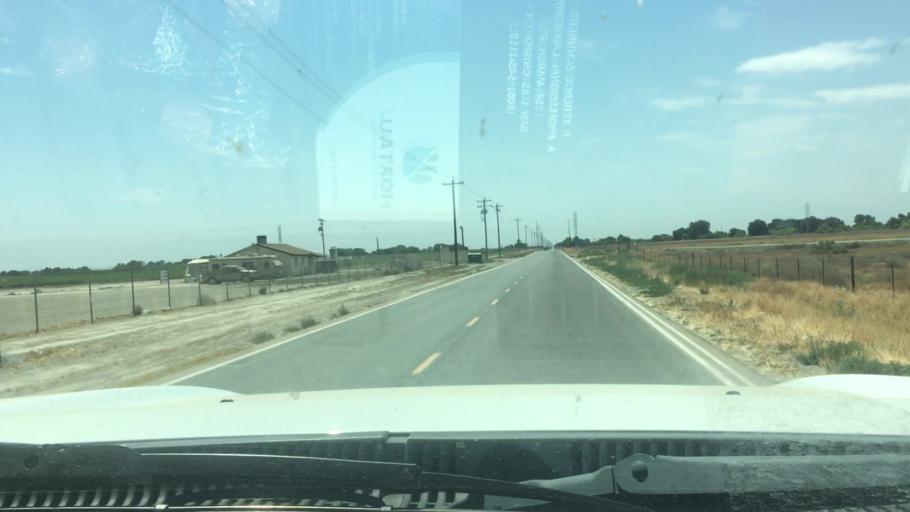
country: US
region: California
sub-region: Kings County
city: Corcoran
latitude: 36.0508
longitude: -119.4897
